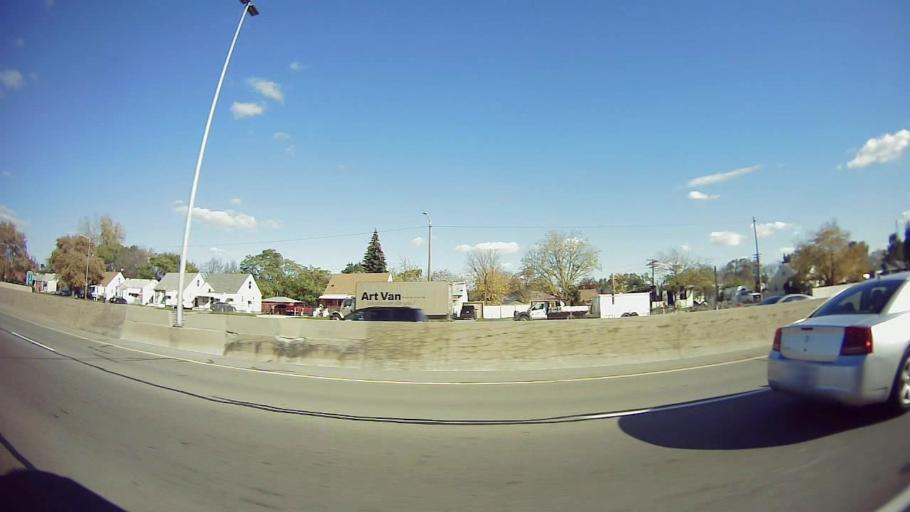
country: US
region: Michigan
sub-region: Wayne County
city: Dearborn
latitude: 42.3404
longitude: -83.2163
